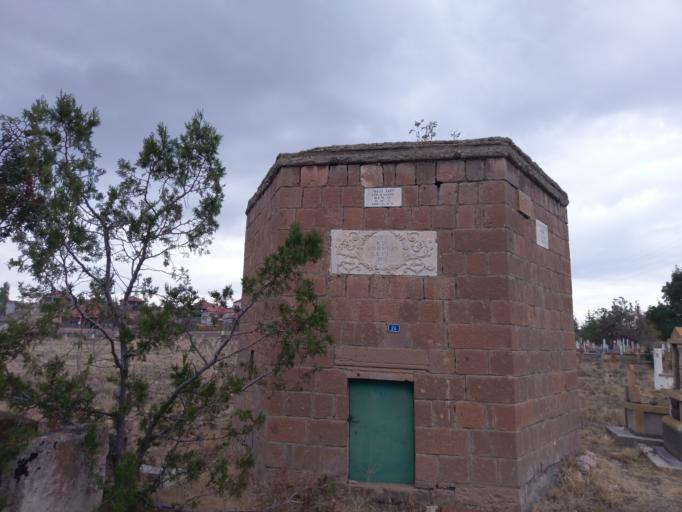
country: TR
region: Kayseri
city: Toklar
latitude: 38.5006
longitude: 36.1187
